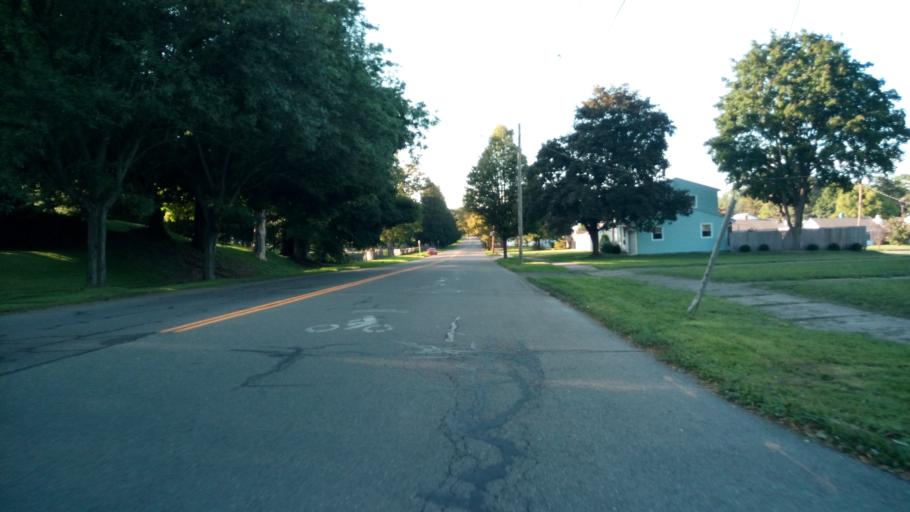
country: US
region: New York
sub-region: Chemung County
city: Elmira
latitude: 42.1044
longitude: -76.8229
